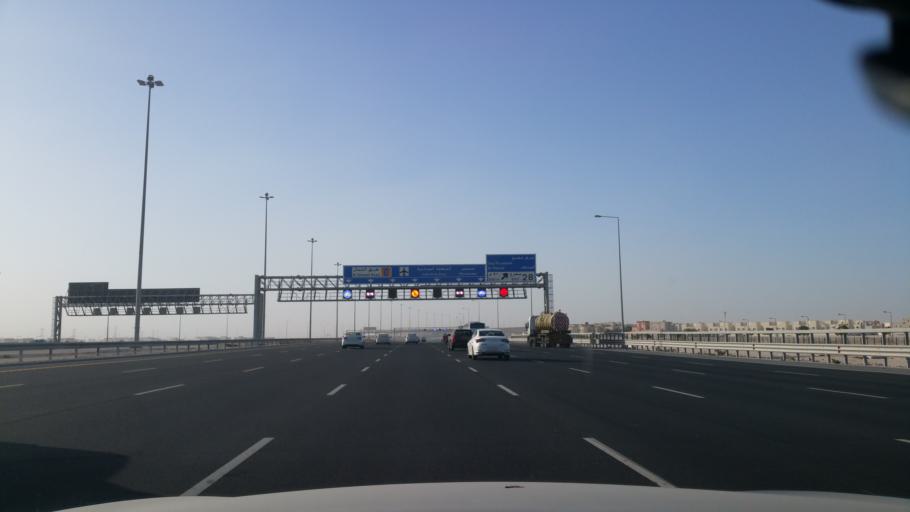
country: QA
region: Al Wakrah
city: Al Wukayr
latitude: 25.1729
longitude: 51.5569
